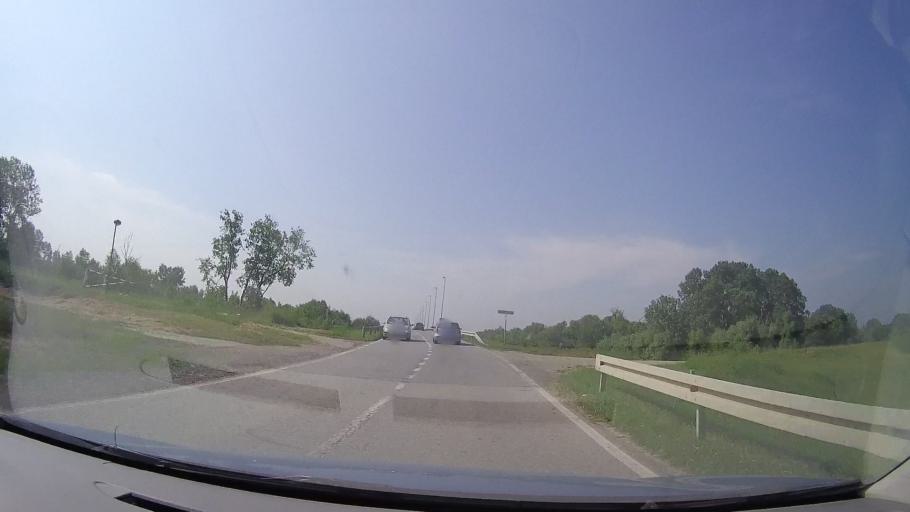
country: RS
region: Autonomna Pokrajina Vojvodina
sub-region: Srednjebanatski Okrug
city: Secanj
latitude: 45.3593
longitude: 20.7710
